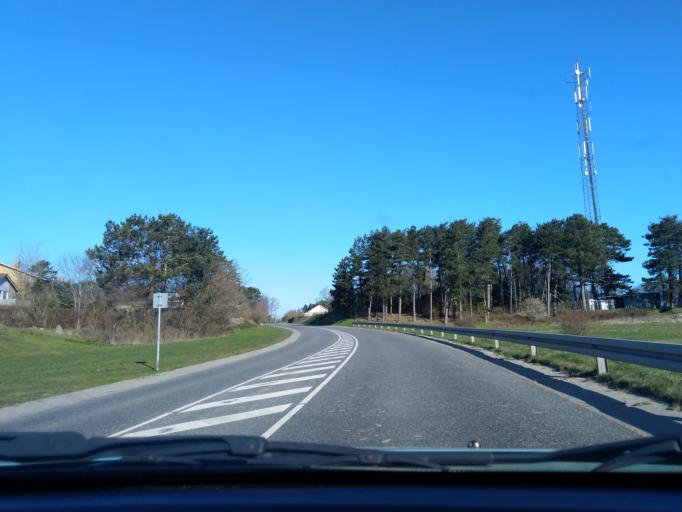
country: DK
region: Zealand
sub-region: Kalundborg Kommune
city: Kalundborg
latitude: 55.7115
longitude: 11.0205
